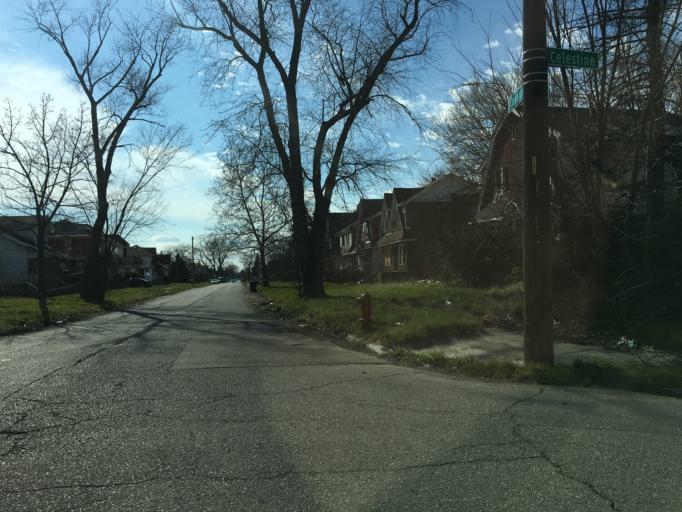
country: US
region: Michigan
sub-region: Macomb County
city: Eastpointe
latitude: 42.4255
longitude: -82.9726
